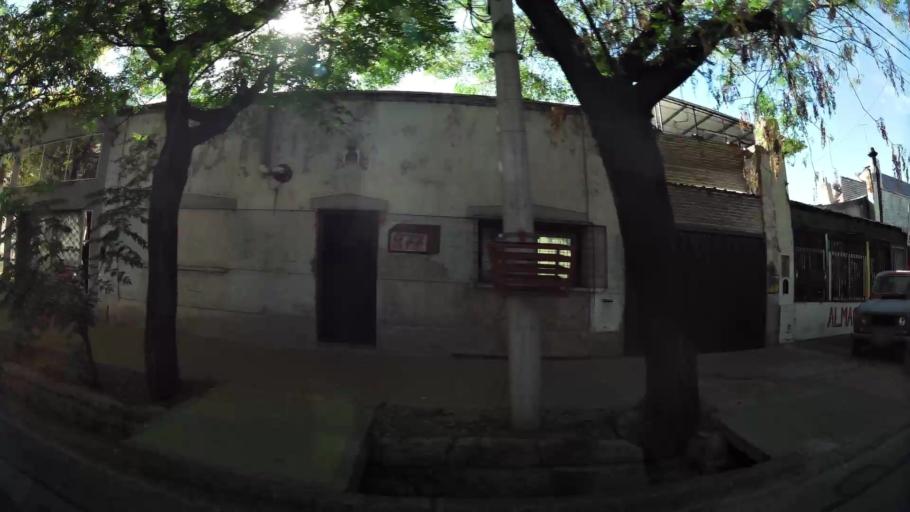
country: AR
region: Mendoza
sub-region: Departamento de Godoy Cruz
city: Godoy Cruz
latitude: -32.9142
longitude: -68.8424
